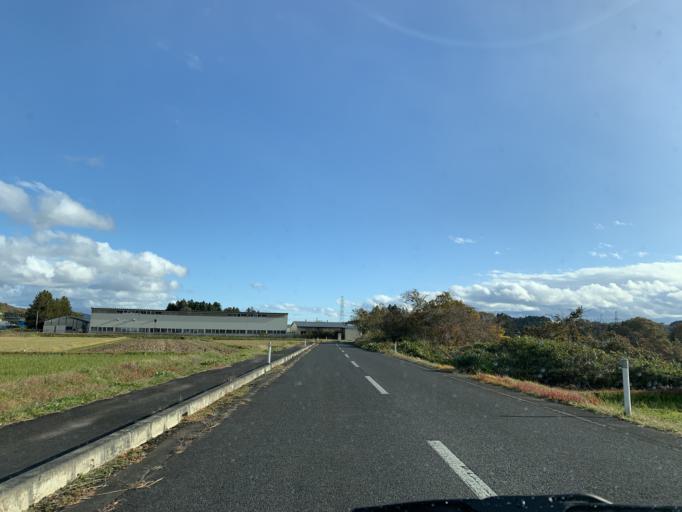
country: JP
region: Iwate
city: Mizusawa
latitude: 39.0286
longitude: 141.0758
